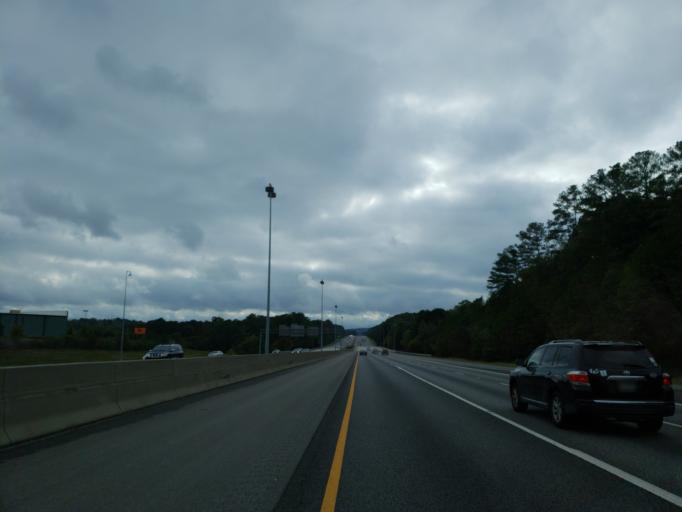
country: US
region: Alabama
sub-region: Jefferson County
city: Hoover
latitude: 33.3812
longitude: -86.8140
